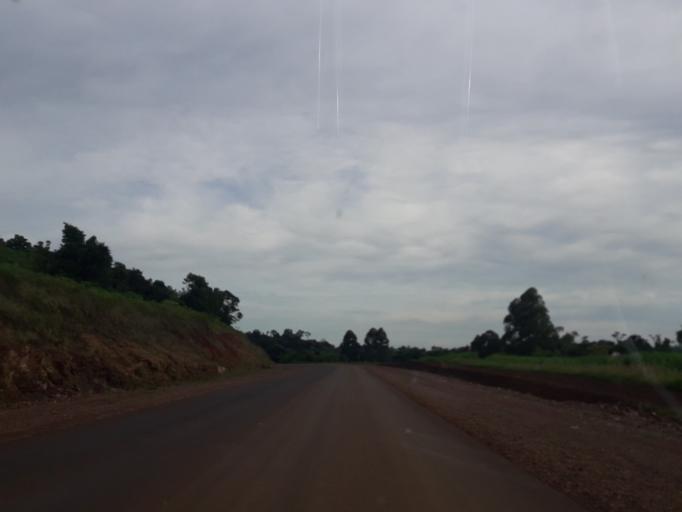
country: AR
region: Misiones
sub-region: Departamento de San Pedro
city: San Pedro
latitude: -26.5327
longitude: -53.9405
